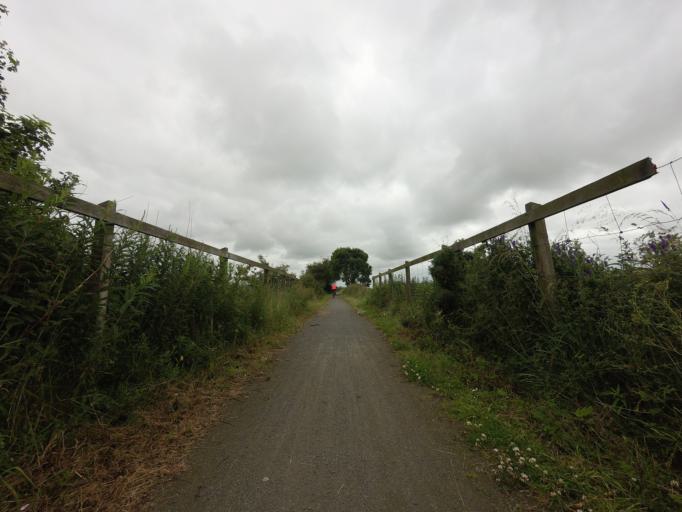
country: GB
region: Scotland
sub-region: Aberdeenshire
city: Ellon
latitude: 57.4736
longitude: -2.1252
